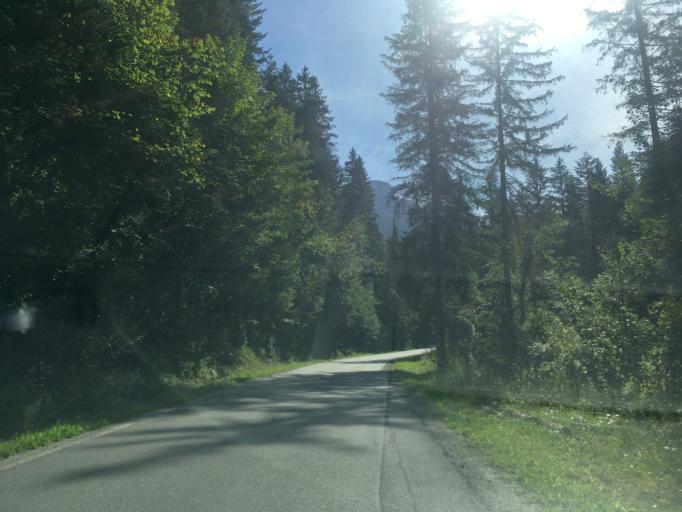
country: AT
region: Salzburg
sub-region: Politischer Bezirk Hallein
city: Abtenau
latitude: 47.5236
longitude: 13.4427
